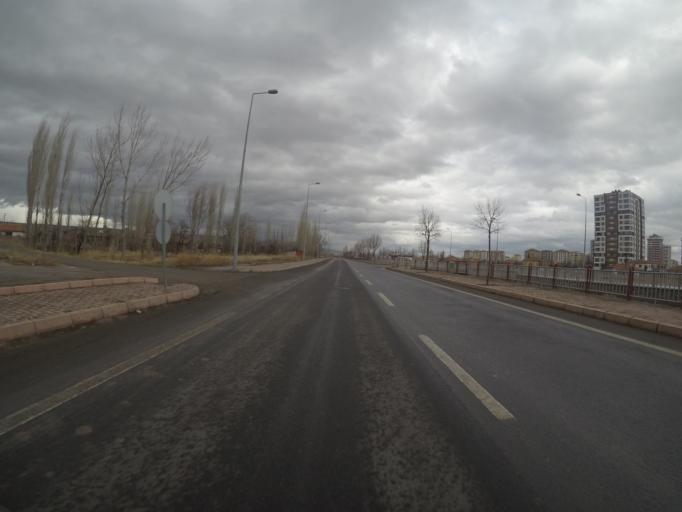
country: TR
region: Kayseri
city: Kayseri
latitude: 38.7519
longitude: 35.4760
